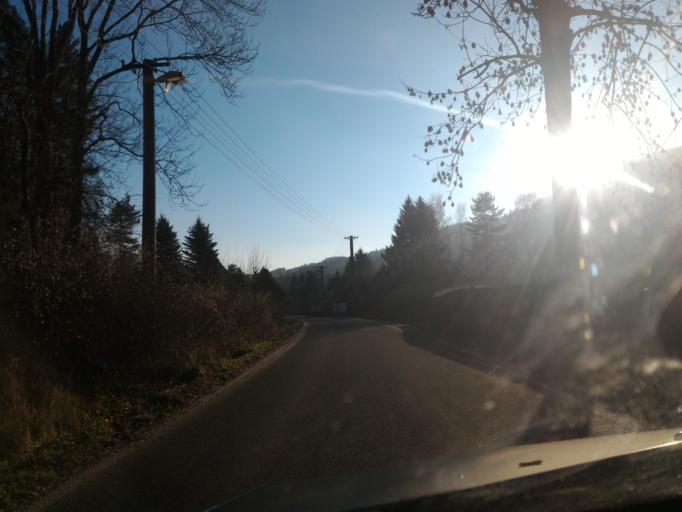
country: DE
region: Saxony
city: Kurort Oybin
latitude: 50.8007
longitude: 14.7191
